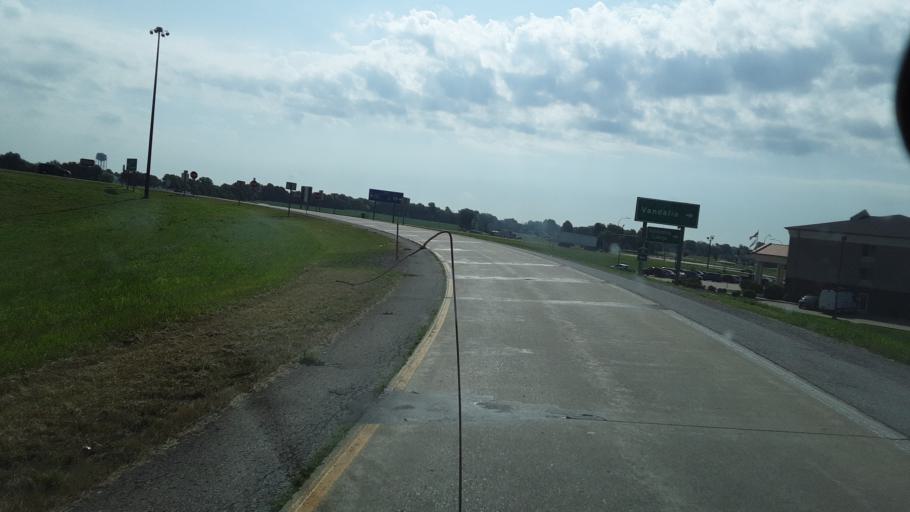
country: US
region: Illinois
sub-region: Fayette County
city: Vandalia
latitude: 38.9679
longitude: -89.1335
